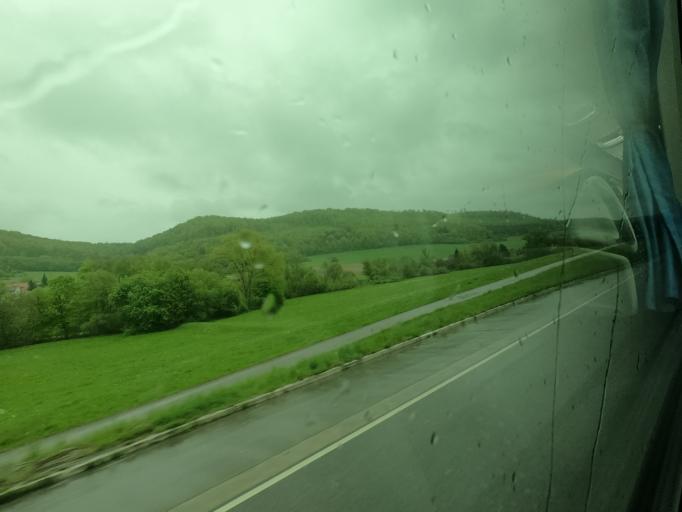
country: DE
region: Baden-Wuerttemberg
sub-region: Regierungsbezirk Stuttgart
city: Oberkochen
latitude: 48.8029
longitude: 10.1253
